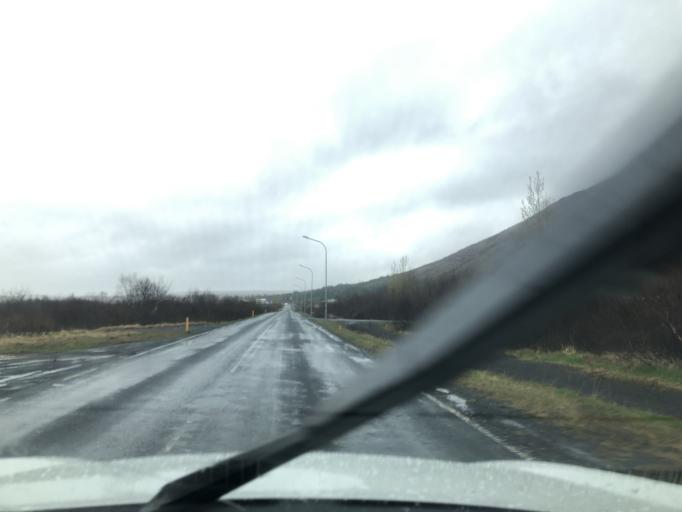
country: IS
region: South
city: Selfoss
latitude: 64.2267
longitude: -20.7214
